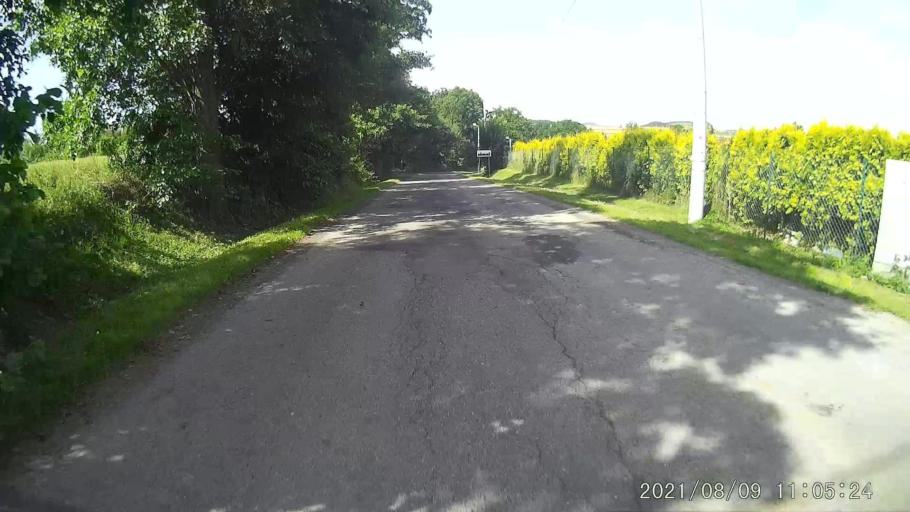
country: PL
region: Lower Silesian Voivodeship
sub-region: Powiat klodzki
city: Bozkow
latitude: 50.4601
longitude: 16.5784
